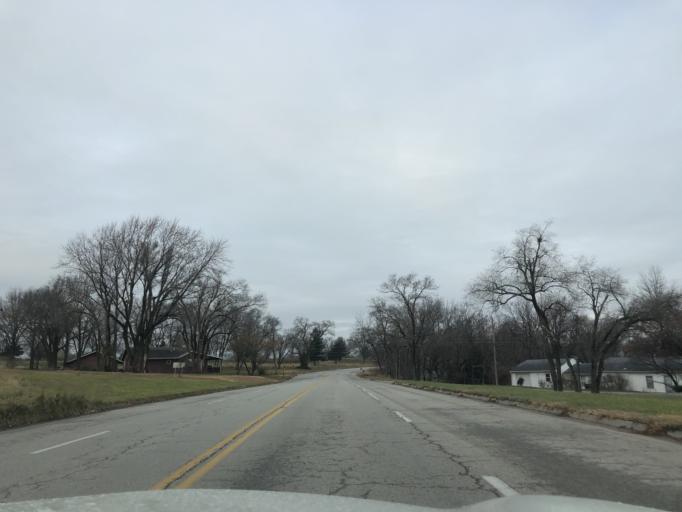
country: US
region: Kansas
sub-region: Johnson County
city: Gardner
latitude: 38.8435
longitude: -94.9284
